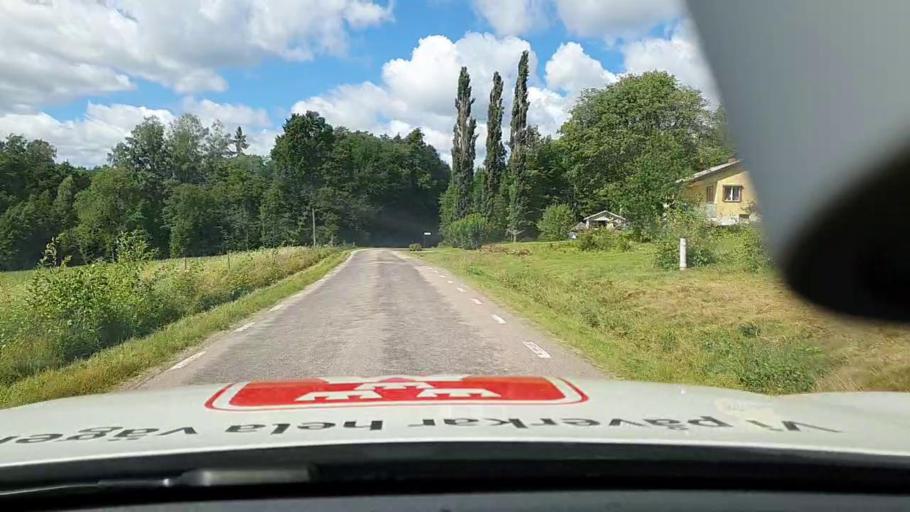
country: SE
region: Vaestra Goetaland
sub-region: Karlsborgs Kommun
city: Molltorp
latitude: 58.5905
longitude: 14.2659
